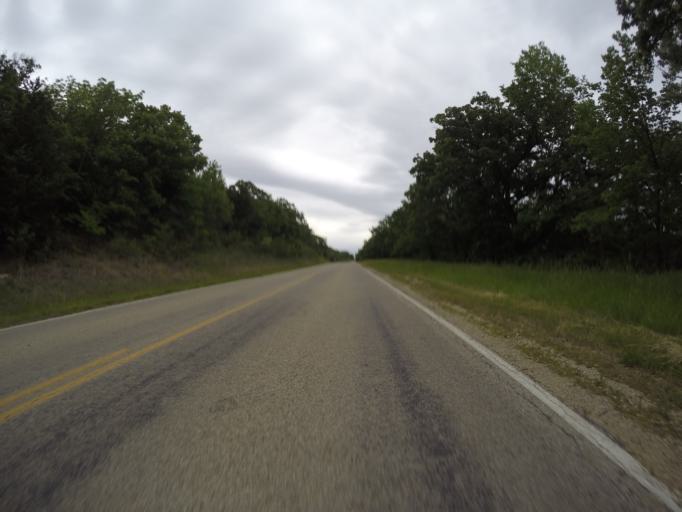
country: US
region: Kansas
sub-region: Pottawatomie County
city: Wamego
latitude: 39.1829
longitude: -96.3607
